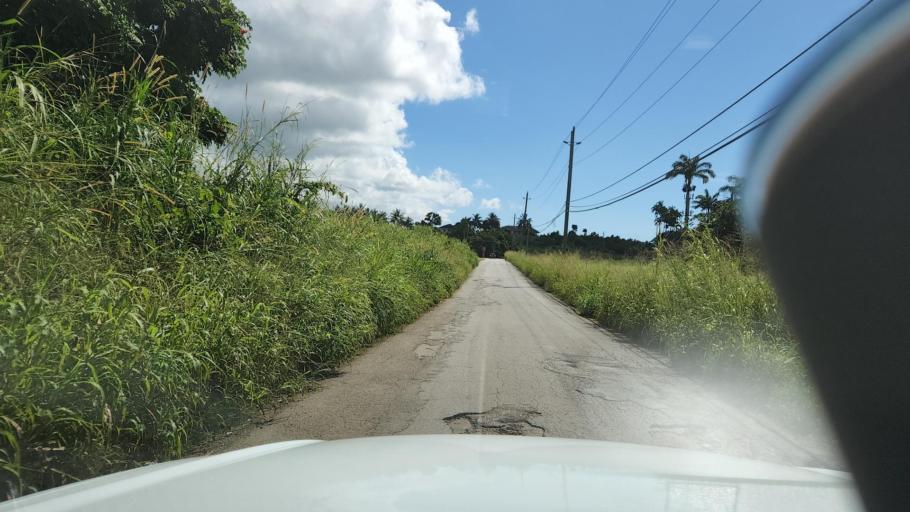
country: BB
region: Saint Thomas
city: Welchman Hall
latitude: 13.1933
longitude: -59.5643
